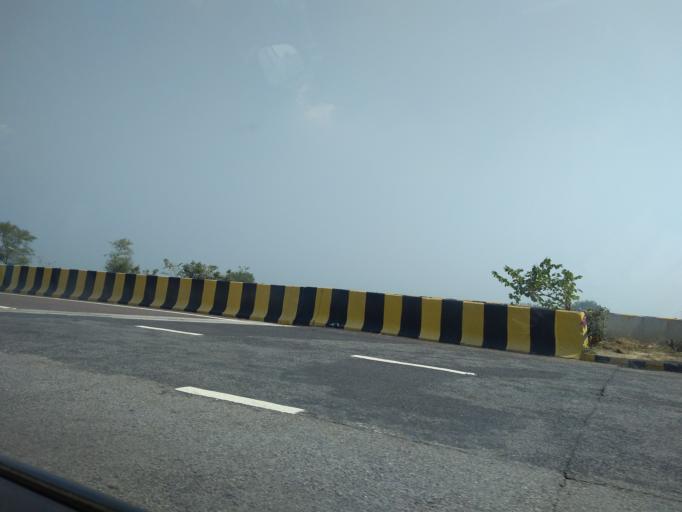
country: IN
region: Uttar Pradesh
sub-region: Mathura
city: Vrindavan
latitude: 27.6146
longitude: 77.7421
